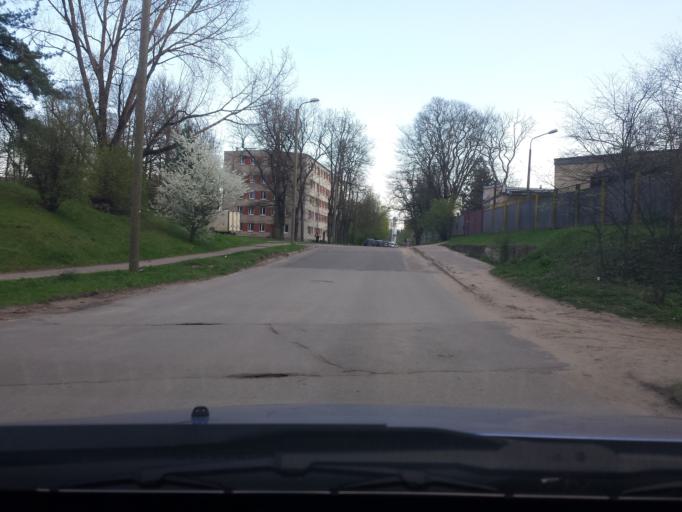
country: LV
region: Riga
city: Jaunciems
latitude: 56.9935
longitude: 24.2278
